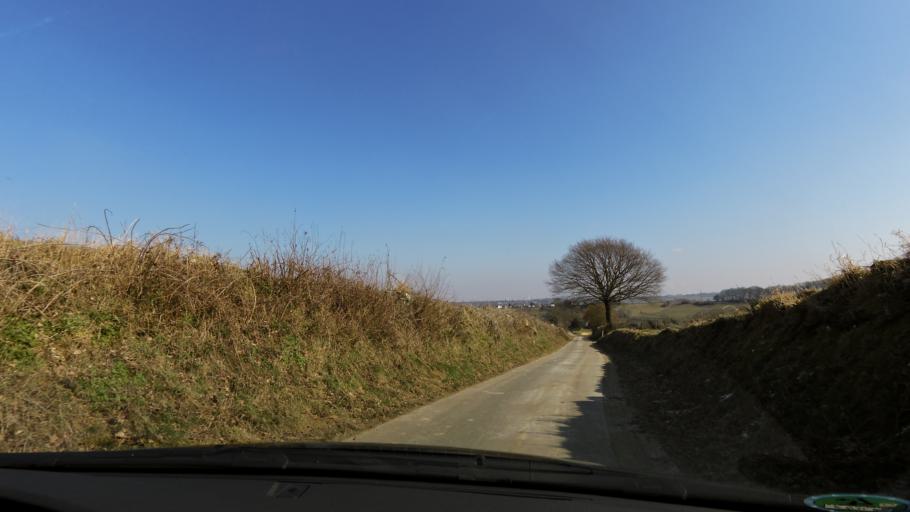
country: BE
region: Wallonia
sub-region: Province de Liege
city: Plombieres
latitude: 50.7787
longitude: 5.9527
